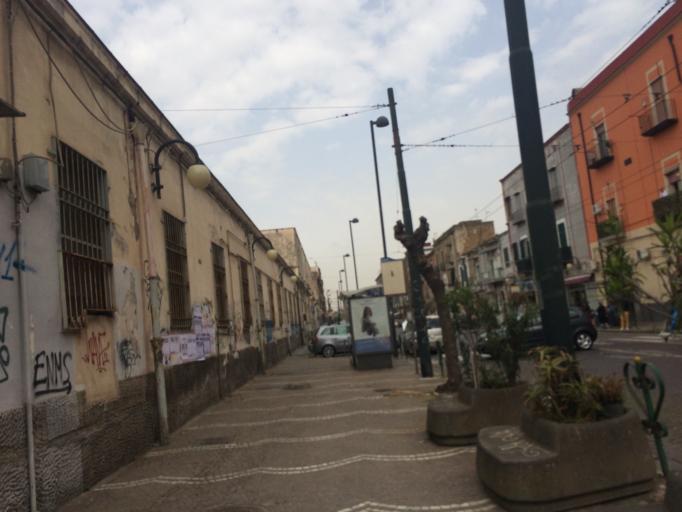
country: IT
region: Campania
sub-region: Provincia di Napoli
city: San Giorgio a Cremano
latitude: 40.8340
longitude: 14.3058
